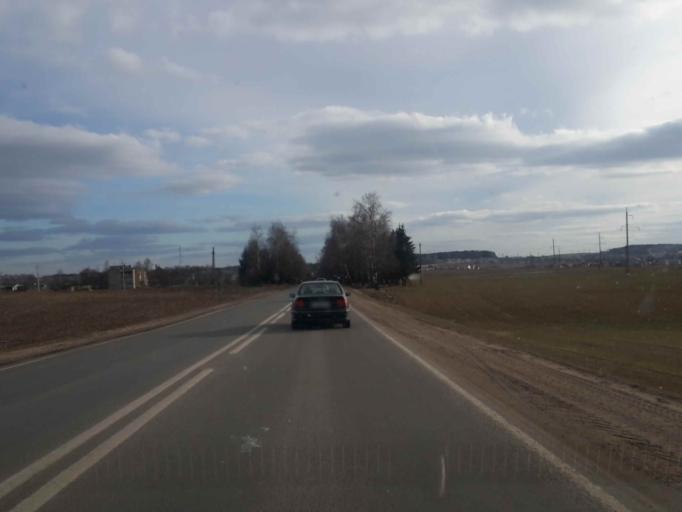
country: BY
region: Minsk
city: Bal'shavik
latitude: 54.0477
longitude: 27.5644
